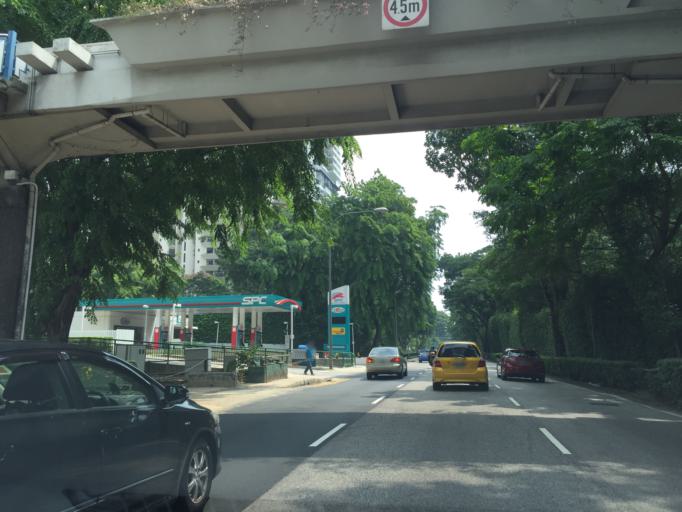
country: SG
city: Singapore
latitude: 1.3181
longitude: 103.8327
